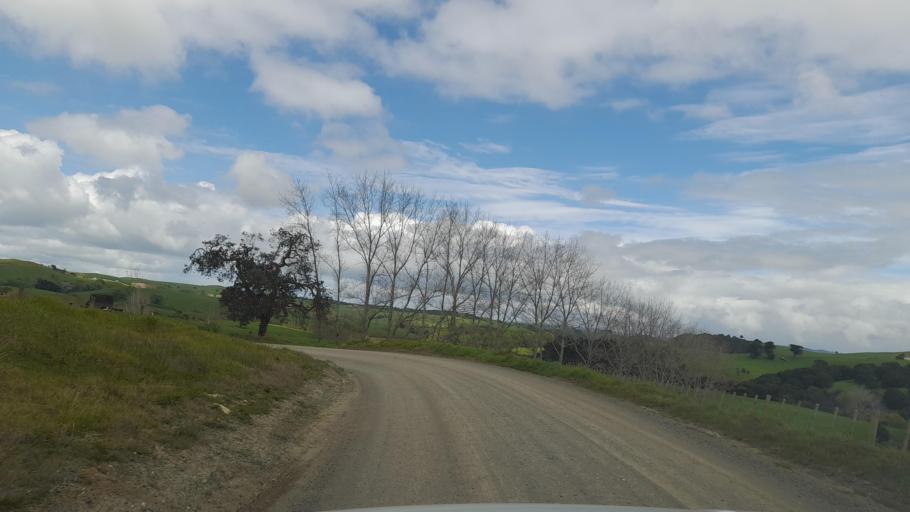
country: NZ
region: Auckland
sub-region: Auckland
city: Wellsford
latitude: -36.1693
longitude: 174.3194
